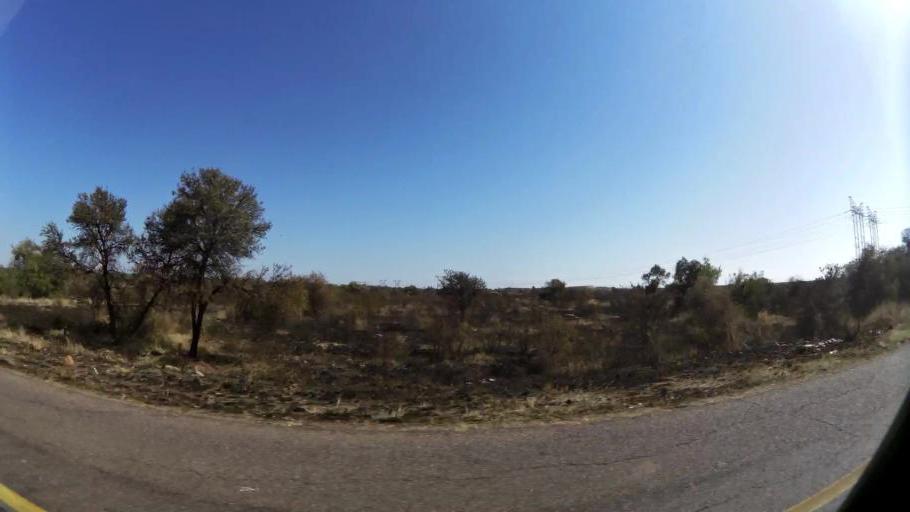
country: ZA
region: Gauteng
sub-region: City of Tshwane Metropolitan Municipality
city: Mabopane
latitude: -25.6146
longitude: 28.1129
